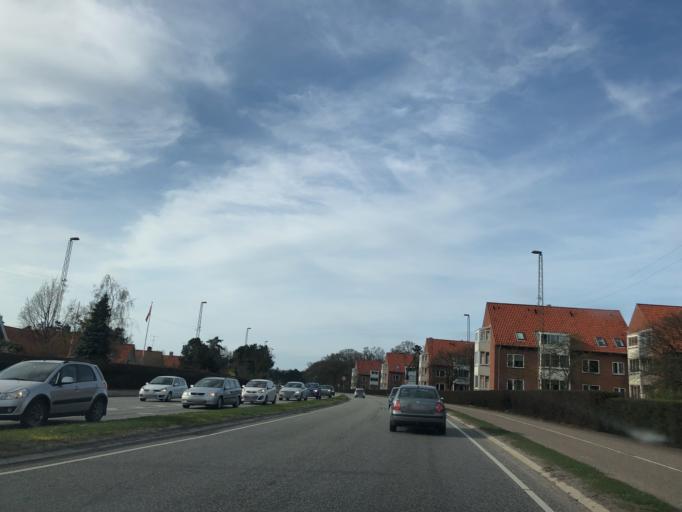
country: DK
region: Zealand
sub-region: Koge Kommune
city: Koge
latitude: 55.4498
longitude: 12.1747
